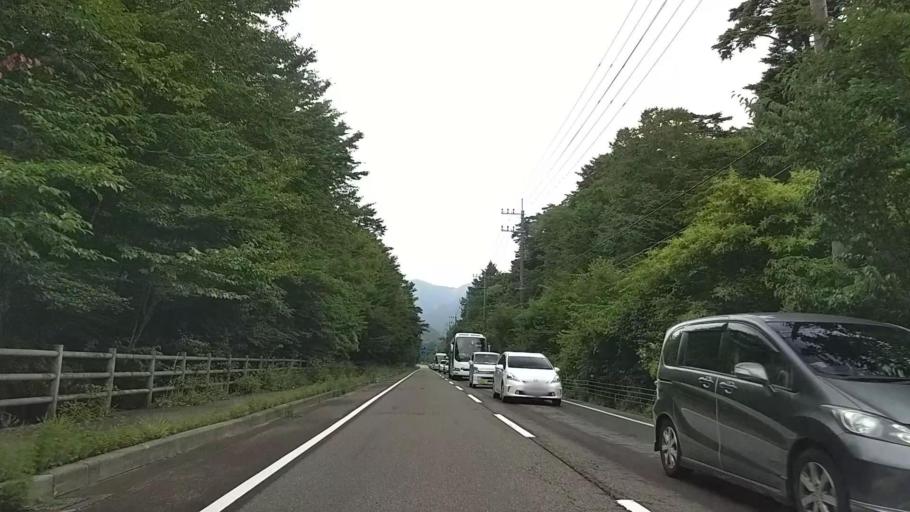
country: JP
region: Yamanashi
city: Fujikawaguchiko
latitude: 35.4851
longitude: 138.6493
